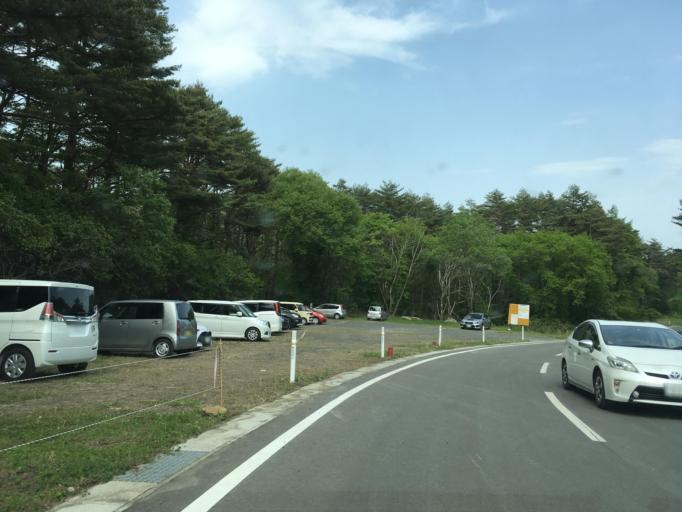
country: JP
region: Iwate
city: Ofunato
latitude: 38.8562
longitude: 141.4708
